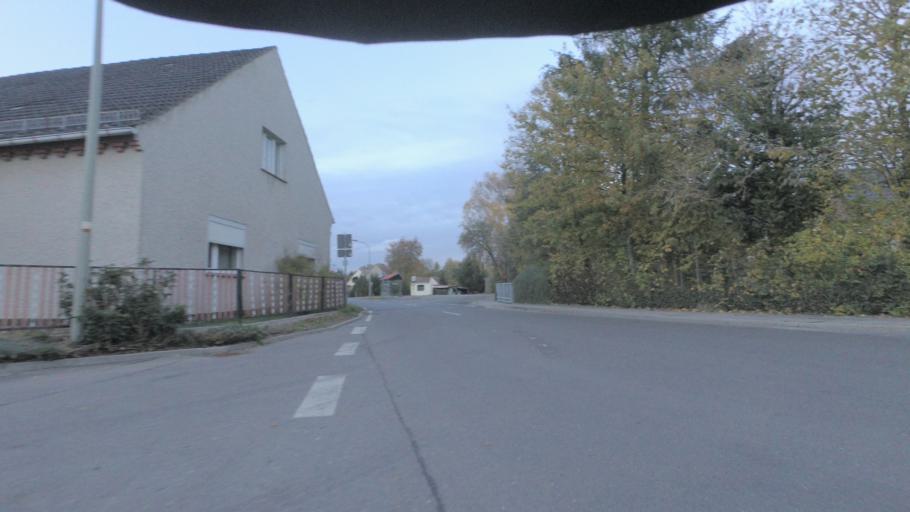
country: DE
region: Brandenburg
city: Sonnewalde
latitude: 51.7559
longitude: 13.6137
